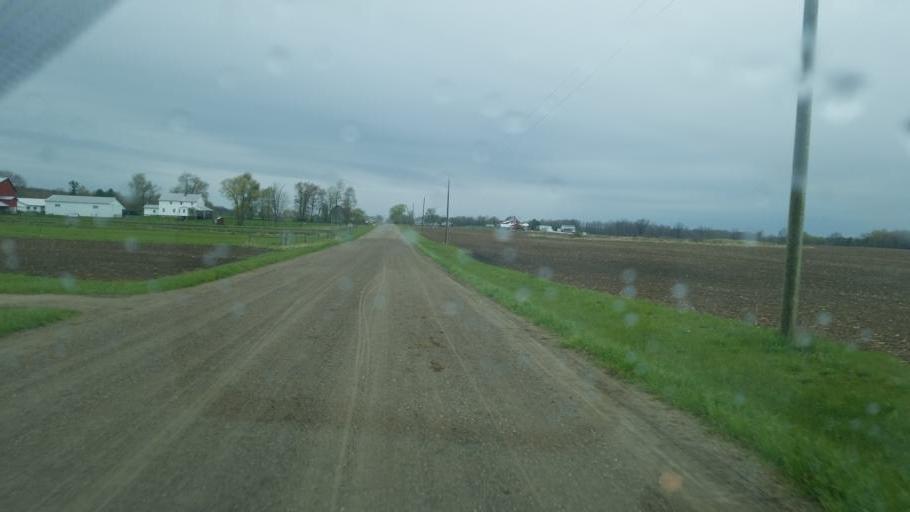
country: US
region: Michigan
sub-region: Montcalm County
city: Lakeview
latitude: 43.5110
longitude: -85.2556
